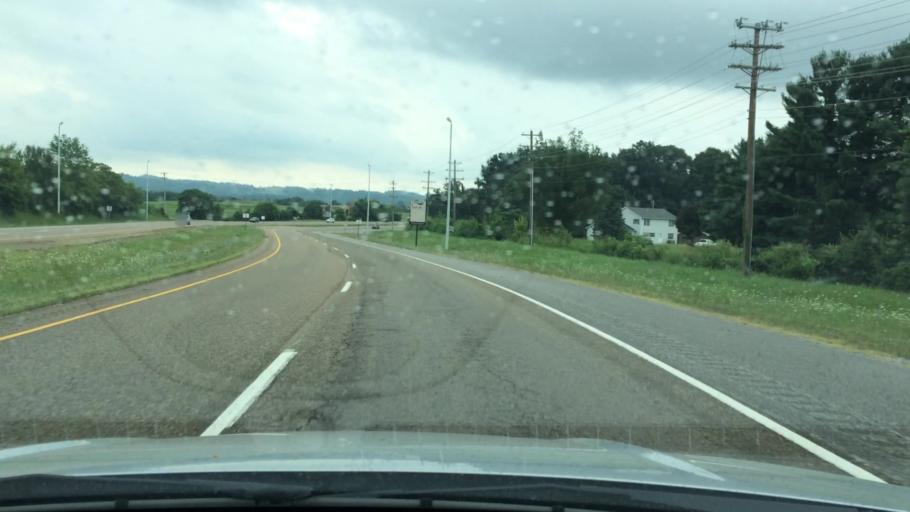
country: US
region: Tennessee
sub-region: Hamblen County
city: Morristown
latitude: 36.1773
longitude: -83.3921
